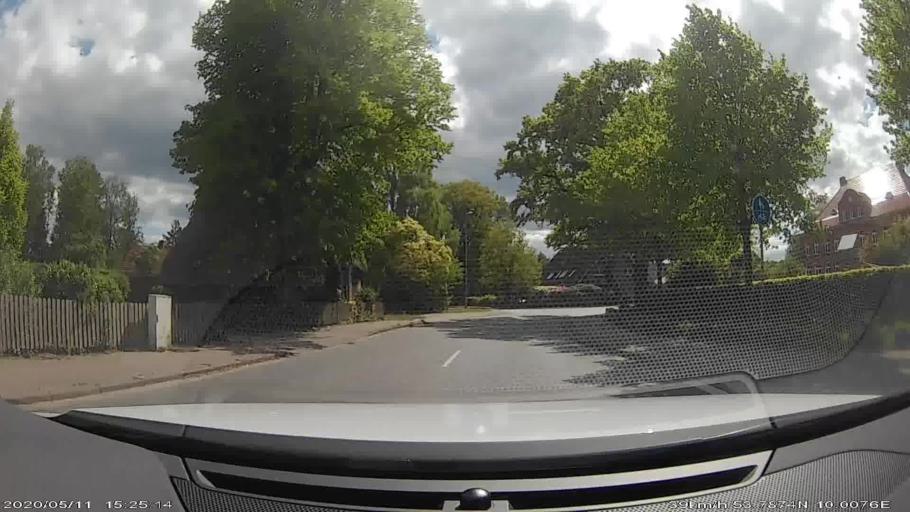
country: DE
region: Schleswig-Holstein
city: Henstedt-Ulzburg
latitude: 53.7873
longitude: 9.9995
